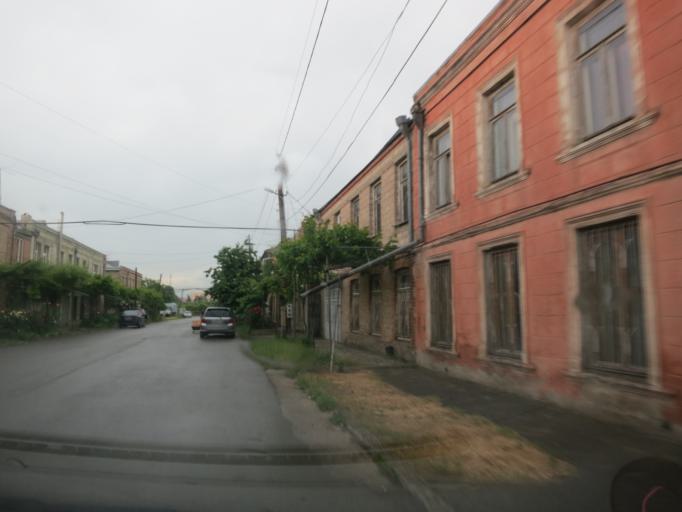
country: GE
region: Shida Kartli
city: Gori
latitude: 41.9900
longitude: 44.1134
